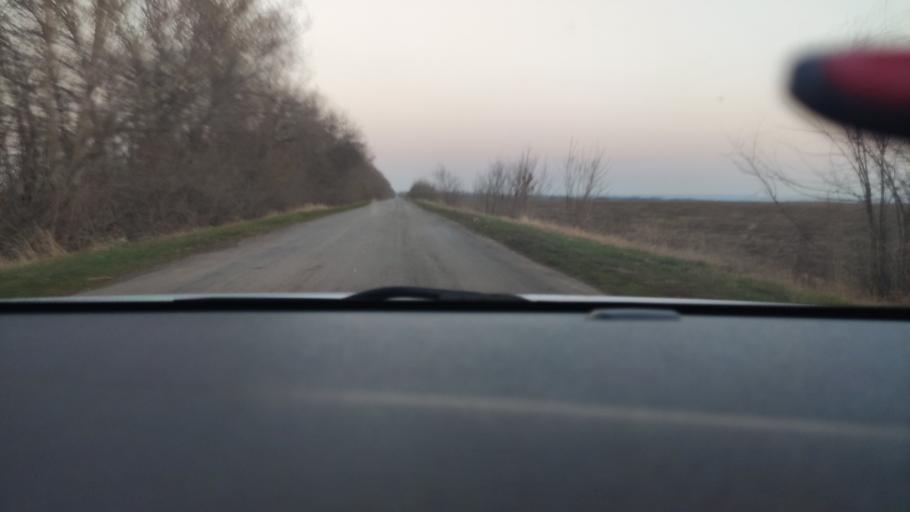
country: RU
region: Voronezj
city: Uryv-Pokrovka
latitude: 51.1452
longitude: 39.0649
